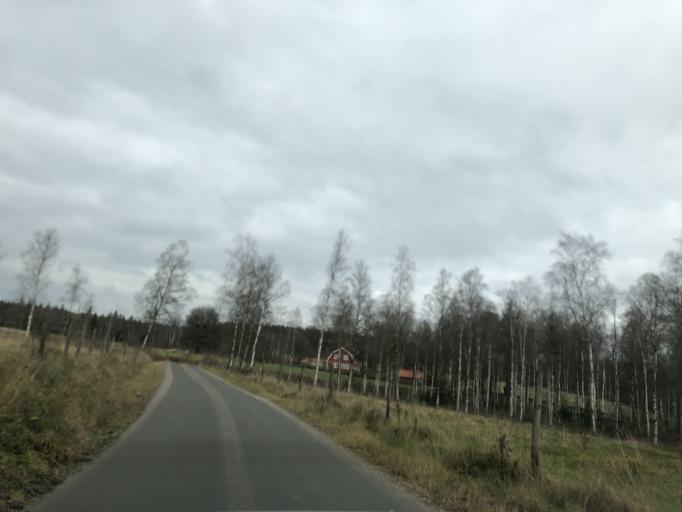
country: SE
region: Vaestra Goetaland
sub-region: Boras Kommun
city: Dalsjofors
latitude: 57.8327
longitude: 13.1742
